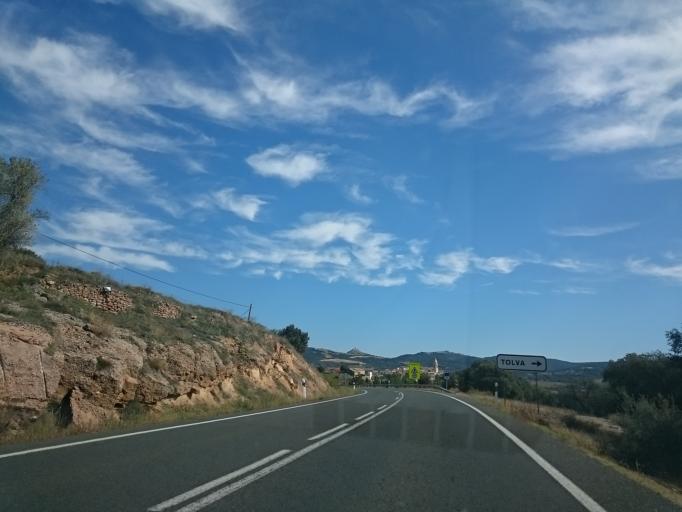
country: ES
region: Aragon
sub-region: Provincia de Huesca
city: Benavarri / Benabarre
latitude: 42.1134
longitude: 0.5566
